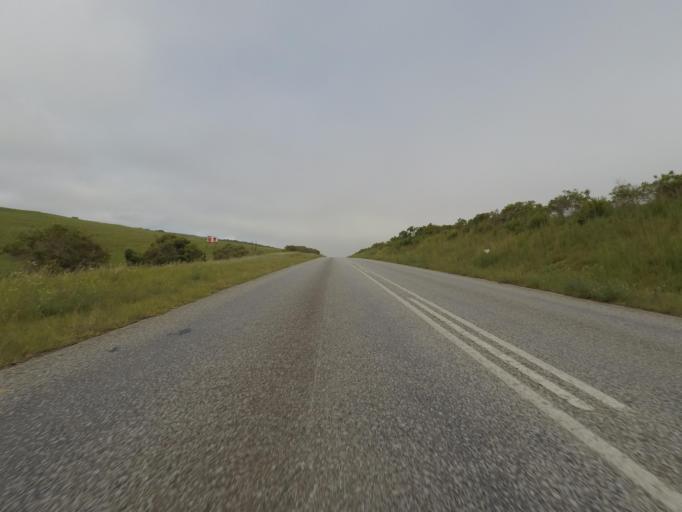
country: ZA
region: Eastern Cape
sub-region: Cacadu District Municipality
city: Port Alfred
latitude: -33.6076
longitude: 26.8198
